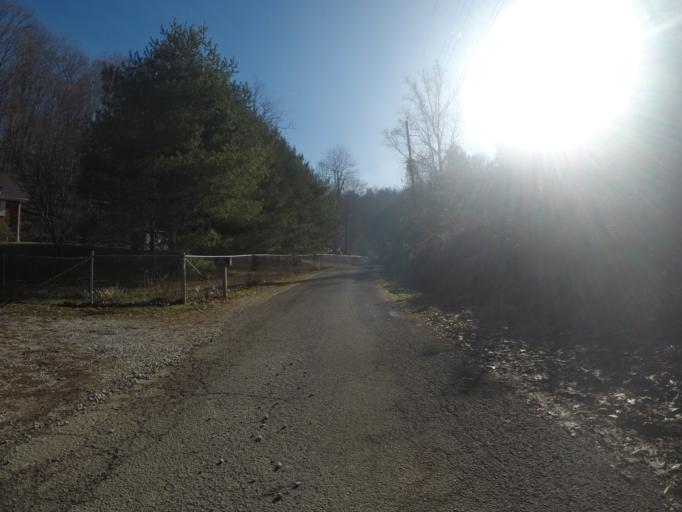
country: US
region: Ohio
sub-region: Lawrence County
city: Burlington
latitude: 38.3924
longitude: -82.4984
